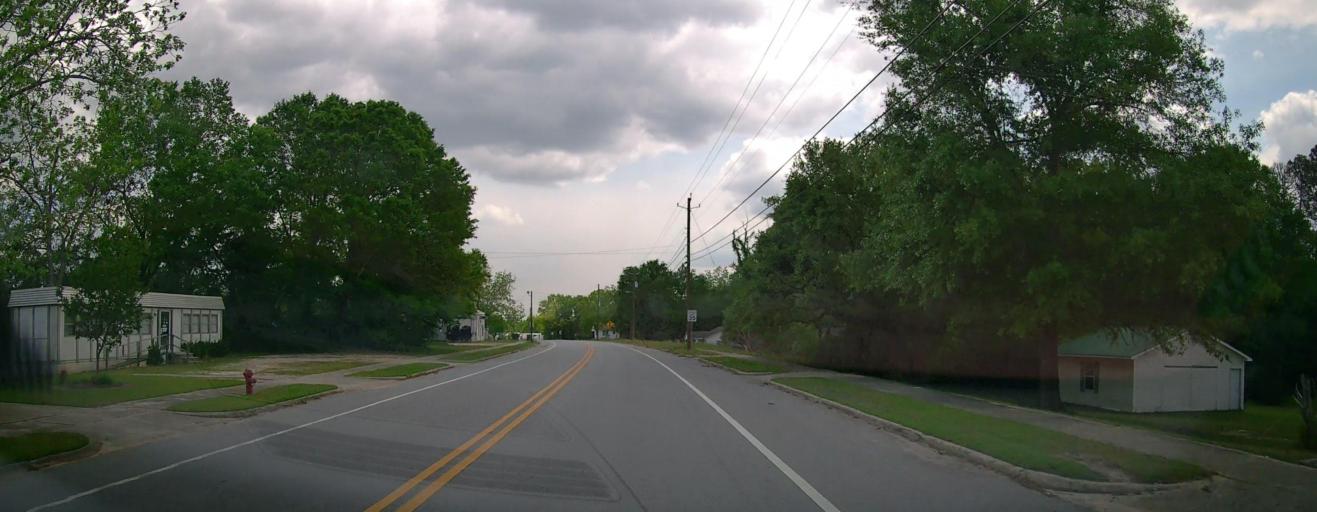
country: US
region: Georgia
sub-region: Treutlen County
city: Soperton
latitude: 32.3827
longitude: -82.5956
